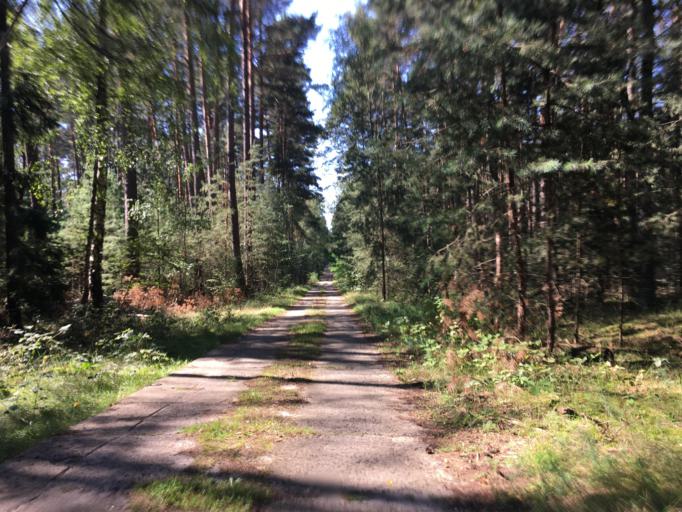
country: DE
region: Brandenburg
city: Gross Koris
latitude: 52.1928
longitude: 13.7218
